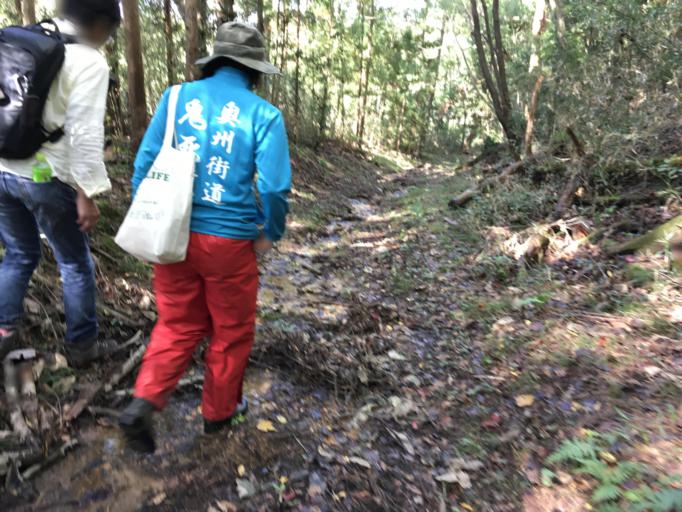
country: JP
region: Iwate
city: Ichinoseki
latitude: 38.8759
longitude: 141.1240
